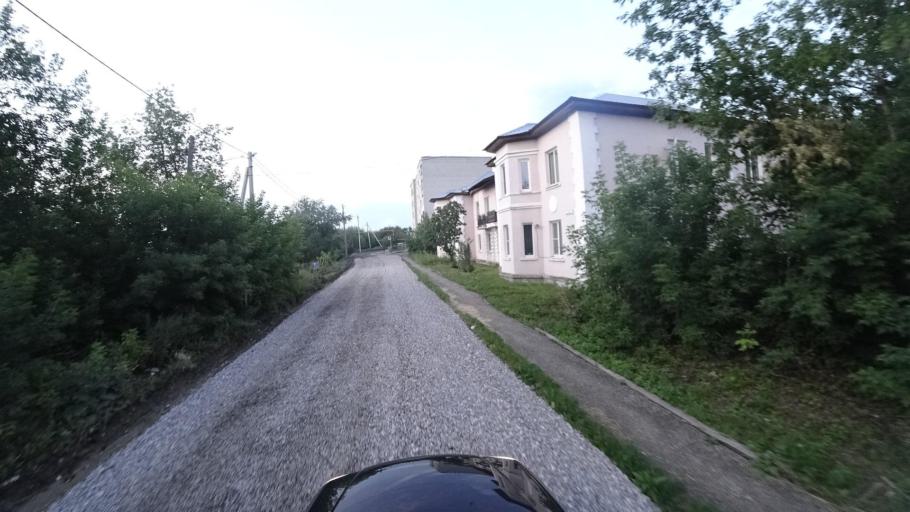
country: RU
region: Sverdlovsk
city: Kamyshlov
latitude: 56.8524
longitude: 62.7092
